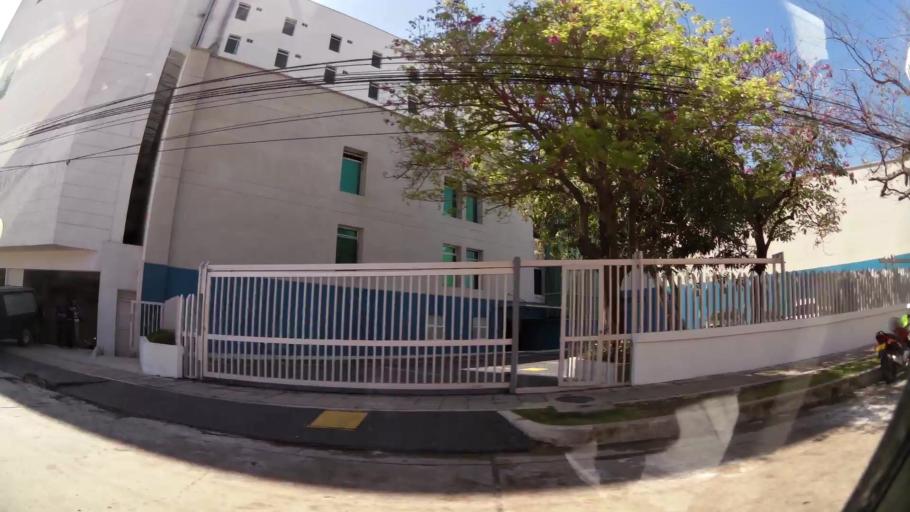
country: CO
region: Atlantico
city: Barranquilla
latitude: 11.0141
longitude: -74.7957
